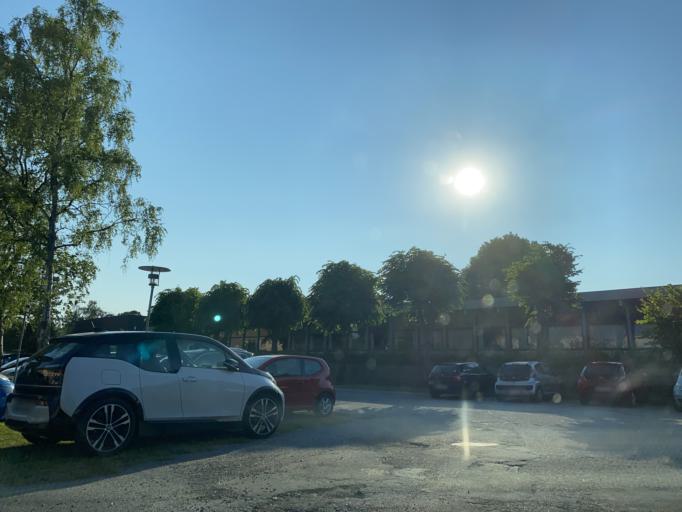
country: DK
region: South Denmark
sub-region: Aabenraa Kommune
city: Aabenraa
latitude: 55.0464
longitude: 9.4111
